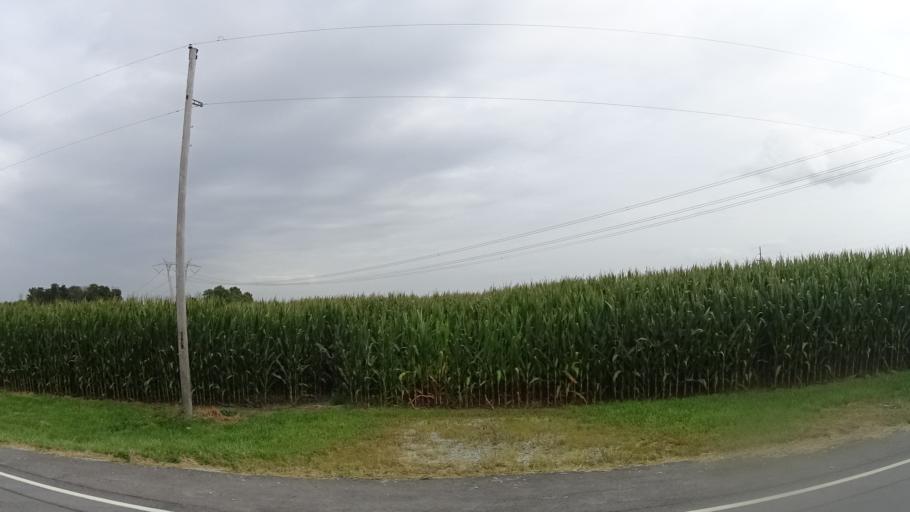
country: US
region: Indiana
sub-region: Madison County
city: Lapel
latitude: 40.0190
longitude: -85.8398
